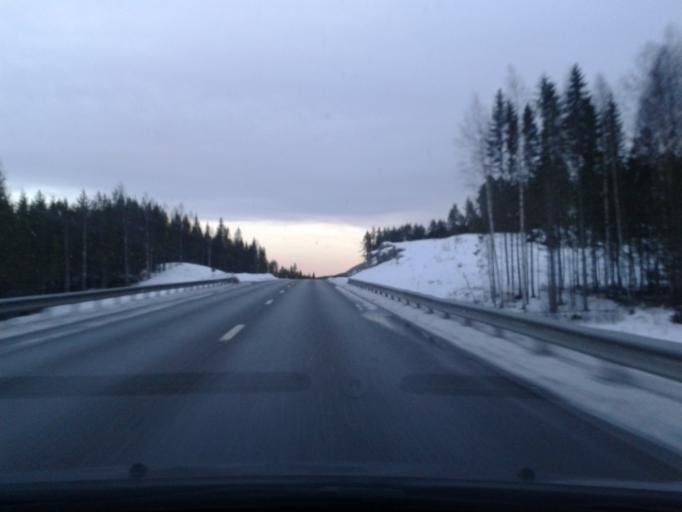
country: SE
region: Vaesternorrland
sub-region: Kramfors Kommun
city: Bollstabruk
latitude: 63.0556
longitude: 17.6124
